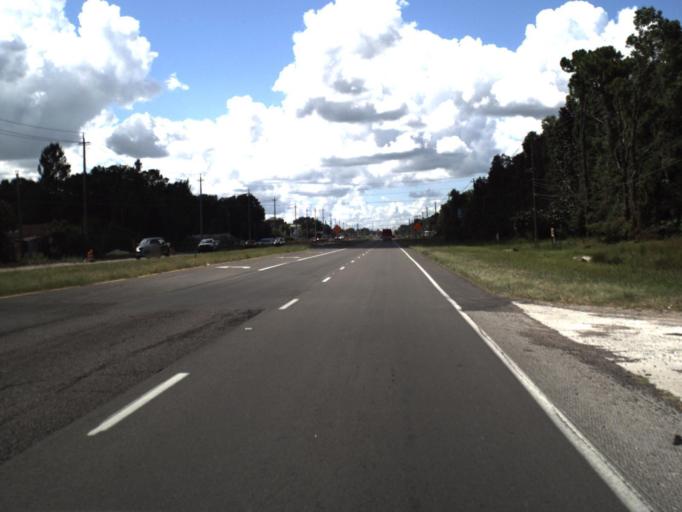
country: US
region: Florida
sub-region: Polk County
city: Gibsonia
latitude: 28.1414
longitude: -81.9738
